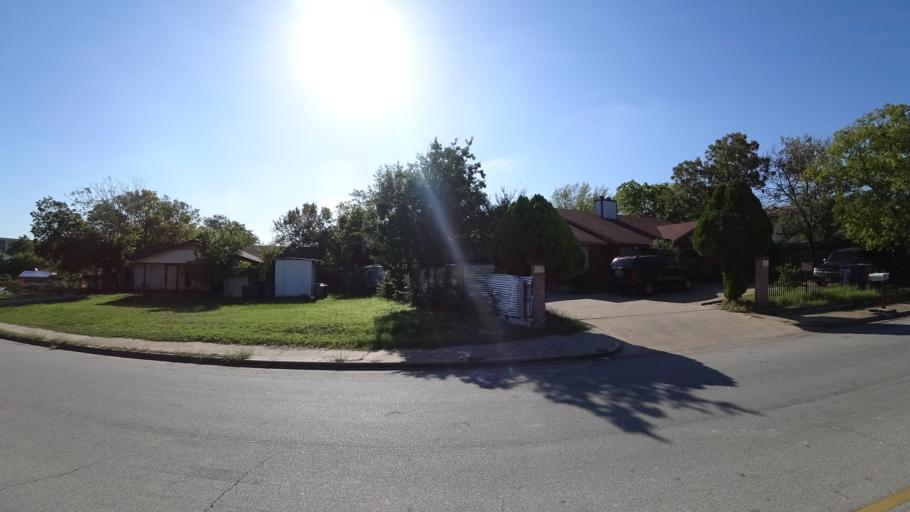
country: US
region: Texas
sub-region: Travis County
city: Austin
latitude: 30.3420
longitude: -97.7071
